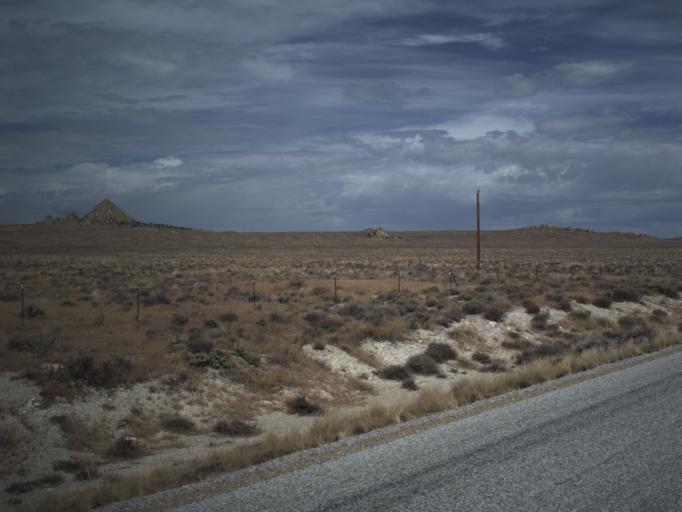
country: US
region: Utah
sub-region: Tooele County
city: Wendover
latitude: 41.4773
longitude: -113.6334
